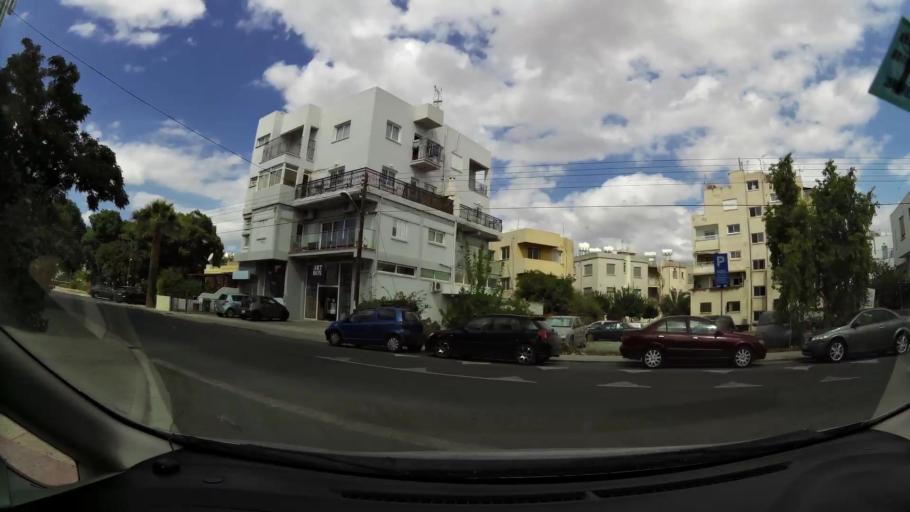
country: CY
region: Lefkosia
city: Nicosia
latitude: 35.1785
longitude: 33.3790
